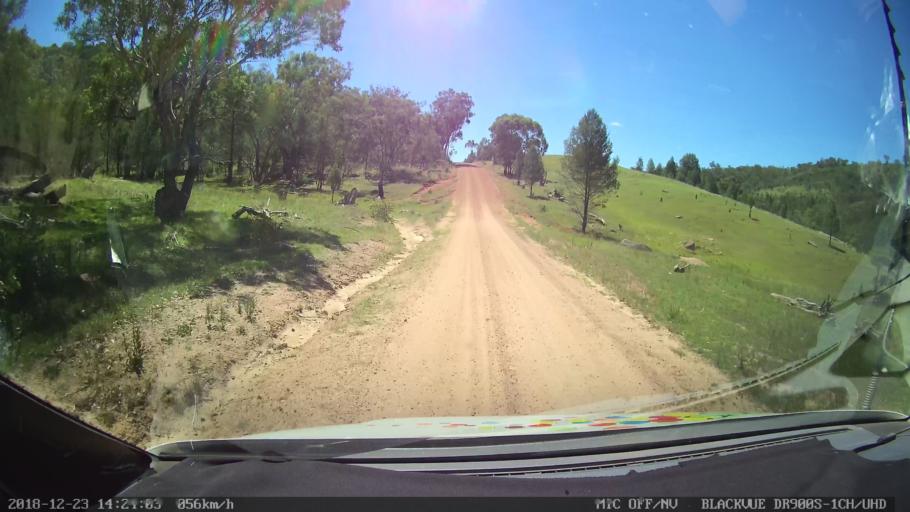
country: AU
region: New South Wales
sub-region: Tamworth Municipality
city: Manilla
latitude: -30.6330
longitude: 150.9635
